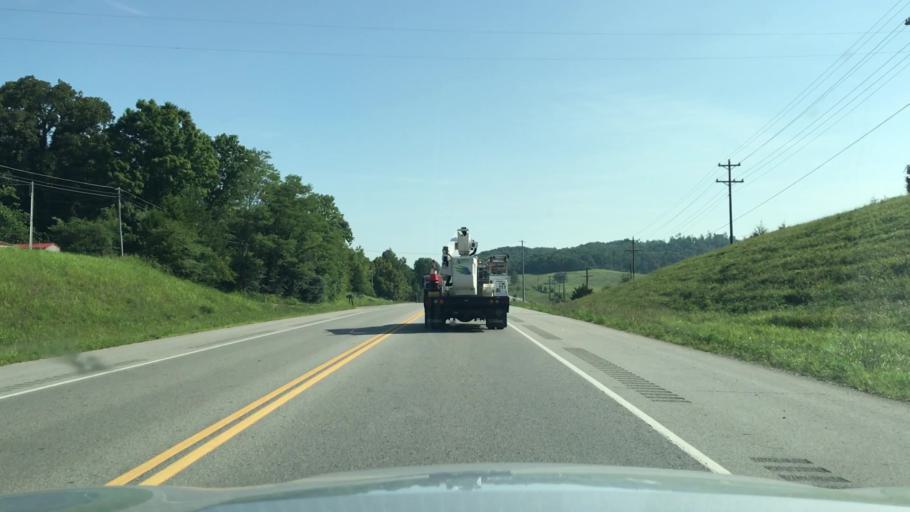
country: US
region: Tennessee
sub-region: Overton County
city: Livingston
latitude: 36.4125
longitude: -85.2878
